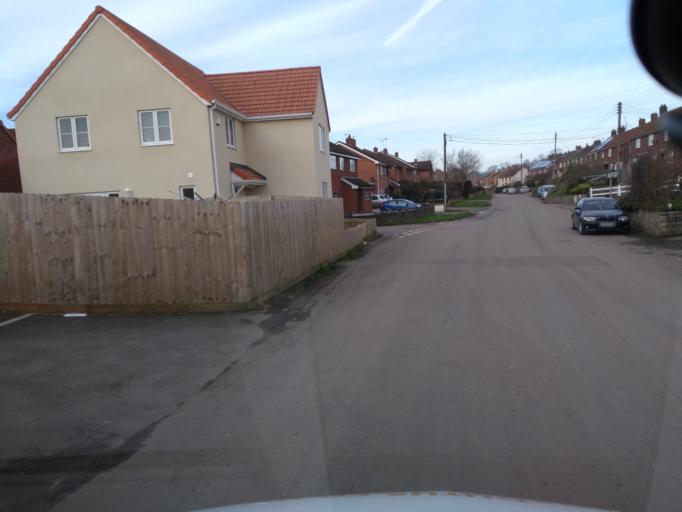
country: GB
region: England
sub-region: Somerset
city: Westonzoyland
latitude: 51.0897
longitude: -2.8943
